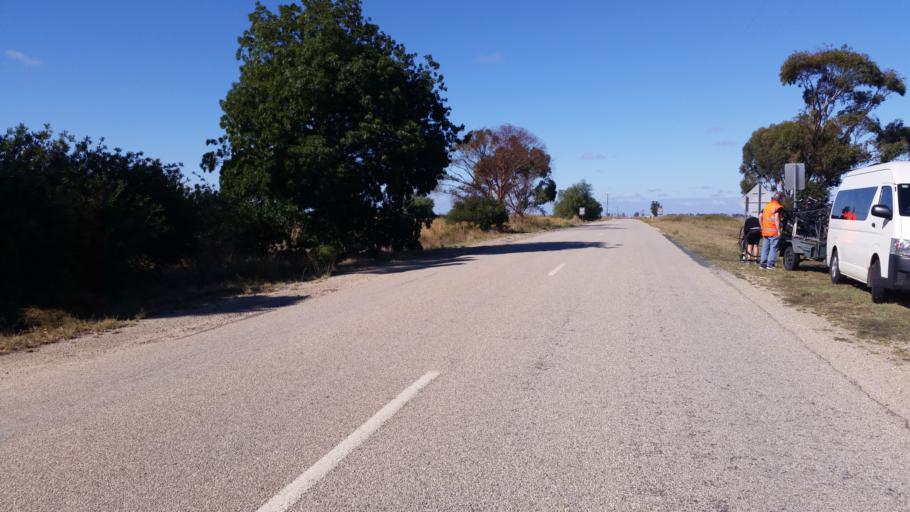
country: AU
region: Victoria
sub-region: Greater Bendigo
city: Epsom
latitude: -36.2120
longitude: 144.2319
